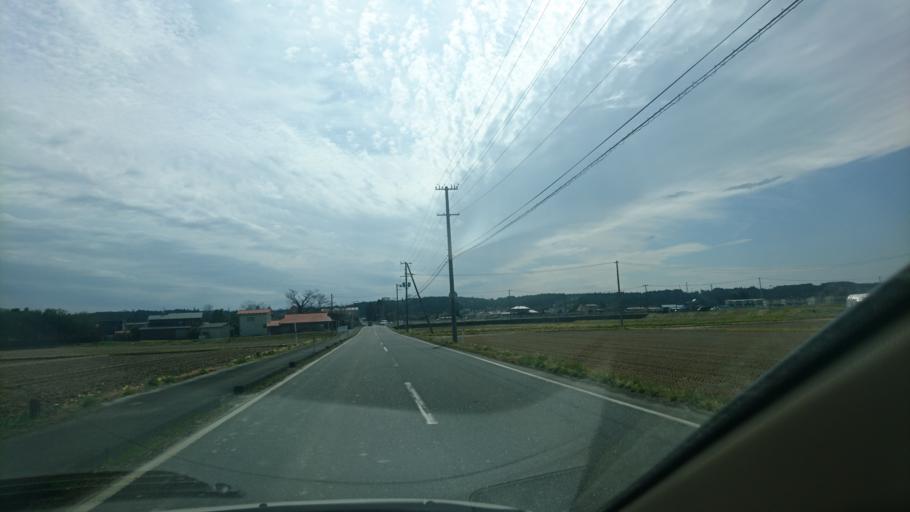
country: JP
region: Miyagi
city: Furukawa
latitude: 38.7449
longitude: 140.9486
